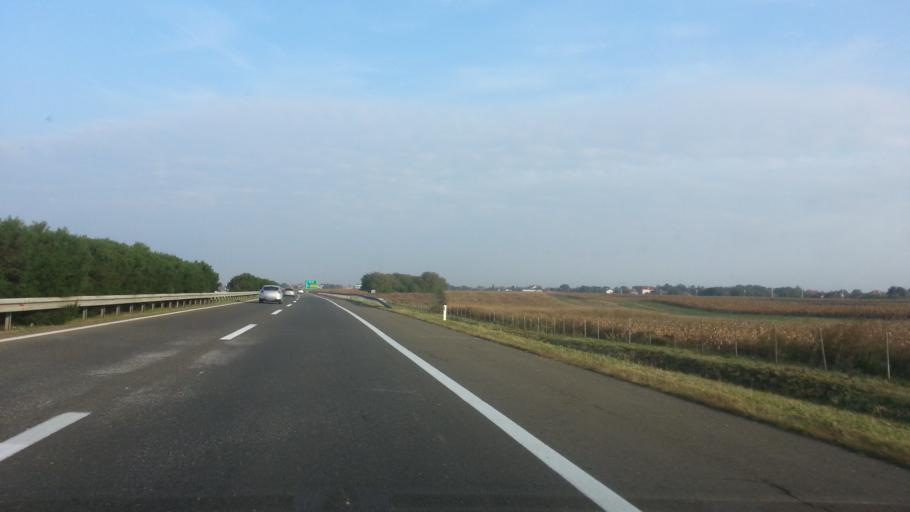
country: RS
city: Novi Banovci
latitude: 44.9335
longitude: 20.2963
